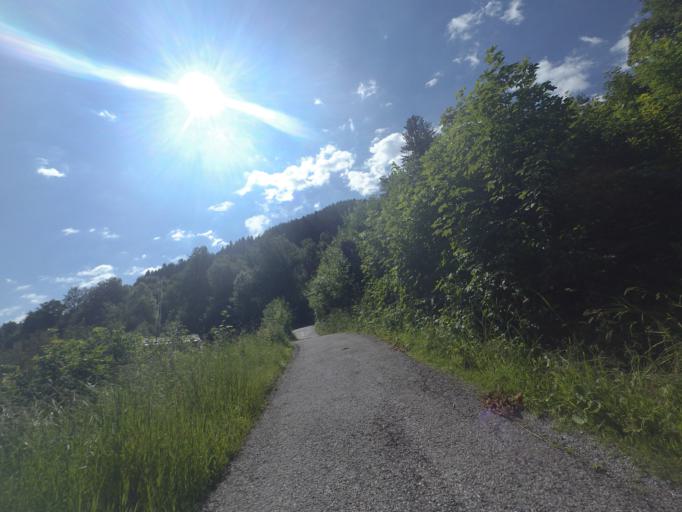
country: AT
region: Salzburg
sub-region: Politischer Bezirk Sankt Johann im Pongau
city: Schwarzach im Pongau
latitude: 47.3113
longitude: 13.1452
